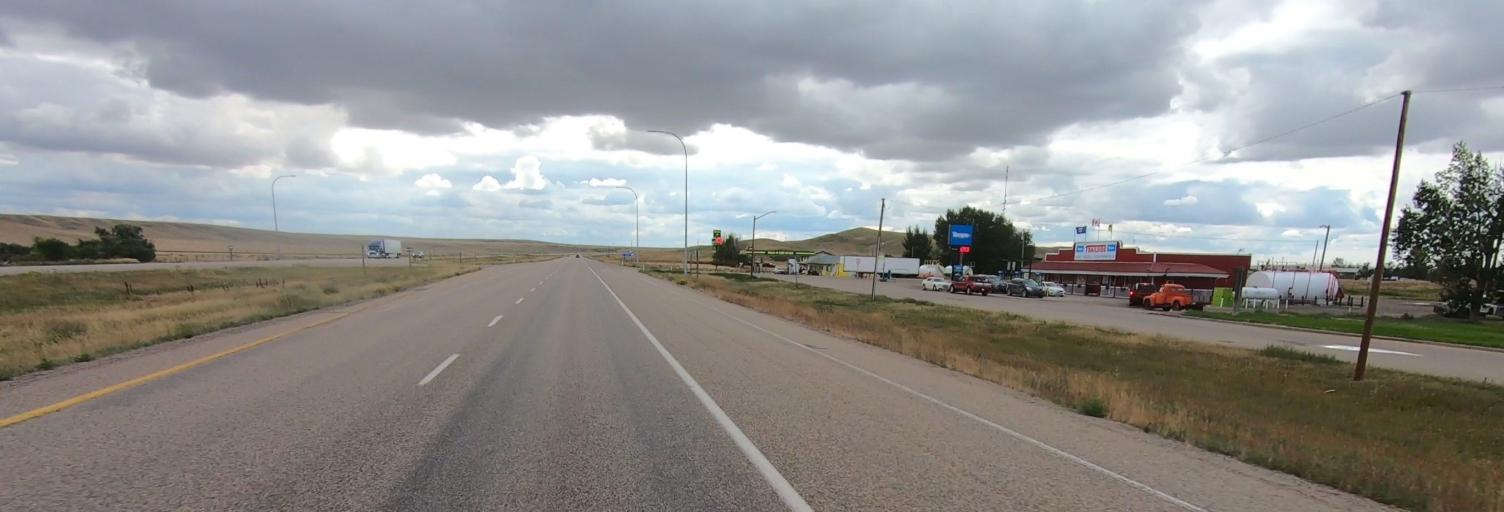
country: CA
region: Saskatchewan
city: Maple Creek
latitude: 49.9433
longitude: -110.0417
